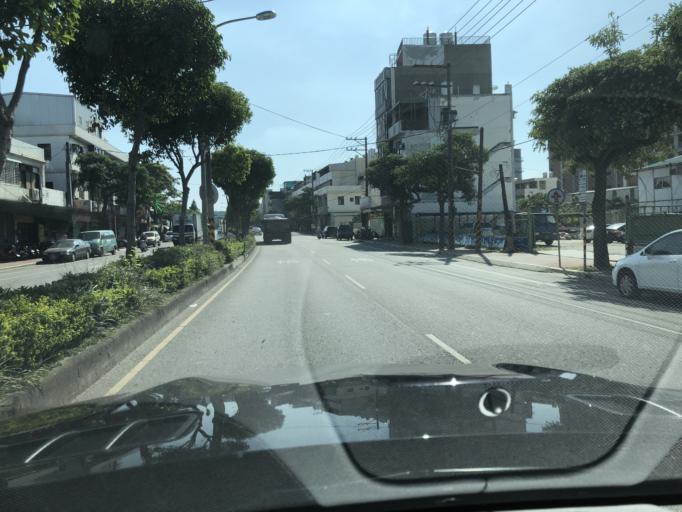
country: TW
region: Taiwan
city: Taoyuan City
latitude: 25.0790
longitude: 121.2856
